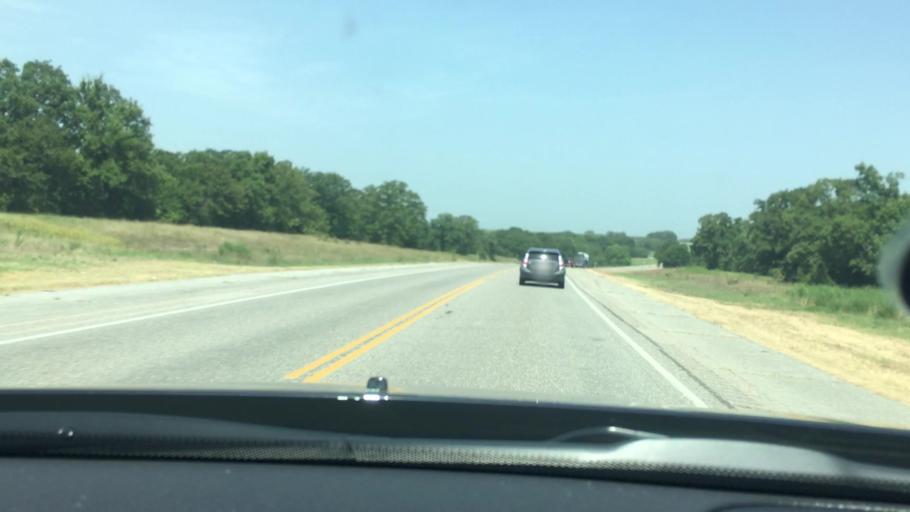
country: US
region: Oklahoma
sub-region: Coal County
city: Coalgate
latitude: 34.6021
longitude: -96.3690
